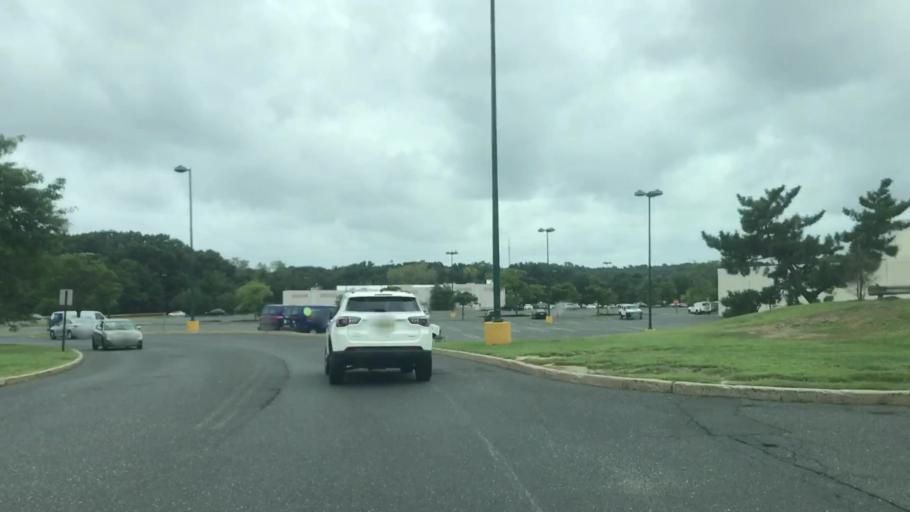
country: US
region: New Jersey
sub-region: Monmouth County
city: Wanamassa
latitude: 40.2330
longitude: -74.0426
